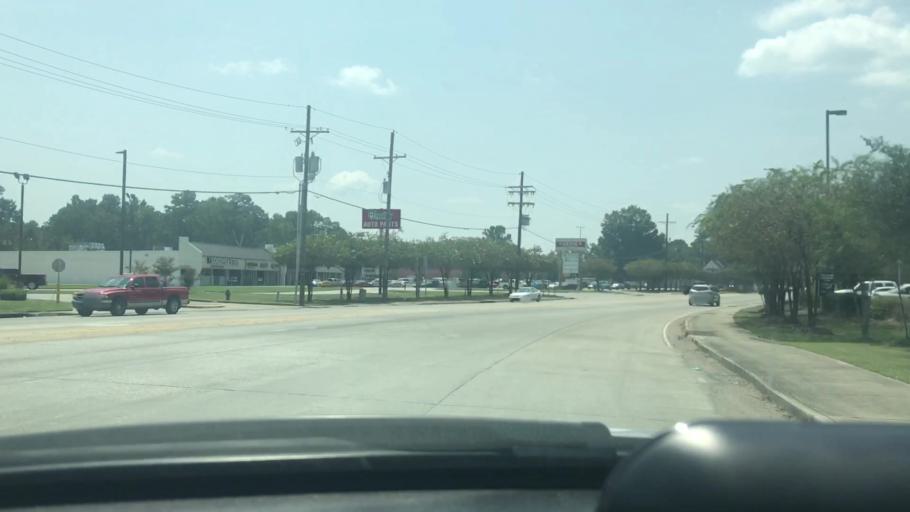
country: US
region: Louisiana
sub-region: Livingston Parish
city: Walker
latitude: 30.4879
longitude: -90.8618
